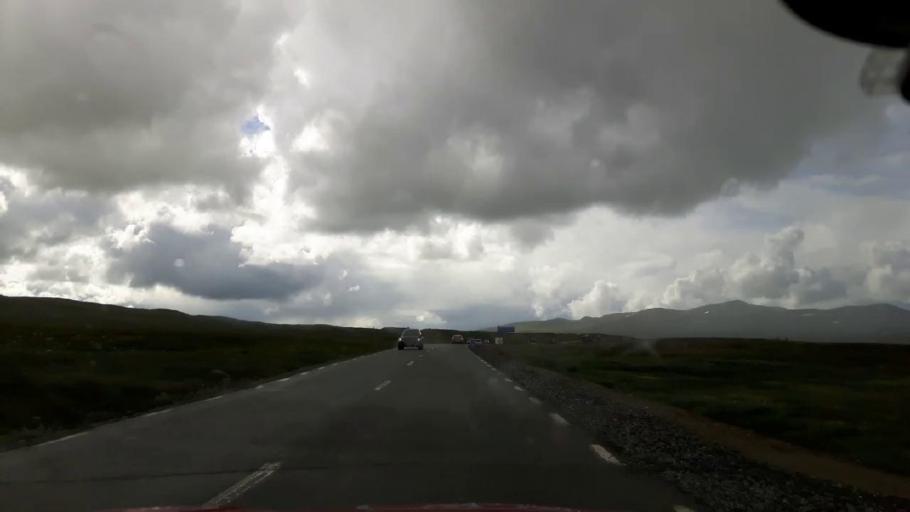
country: NO
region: Nordland
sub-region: Hattfjelldal
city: Hattfjelldal
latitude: 65.0978
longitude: 14.4671
